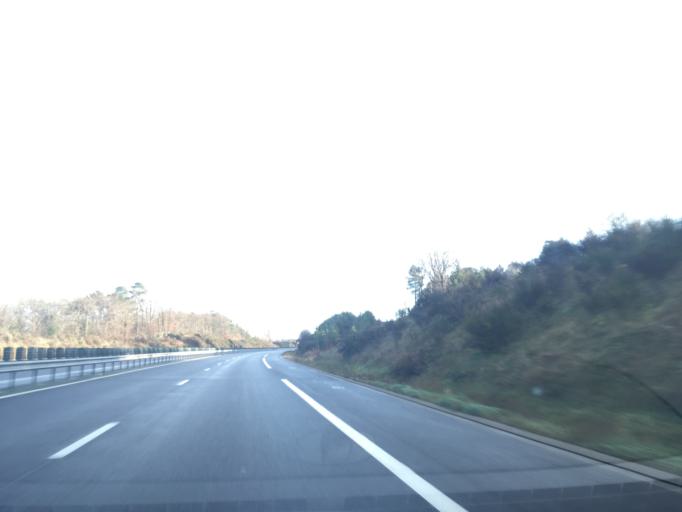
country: FR
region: Limousin
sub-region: Departement de la Correze
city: Cublac
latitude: 45.1716
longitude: 1.2994
